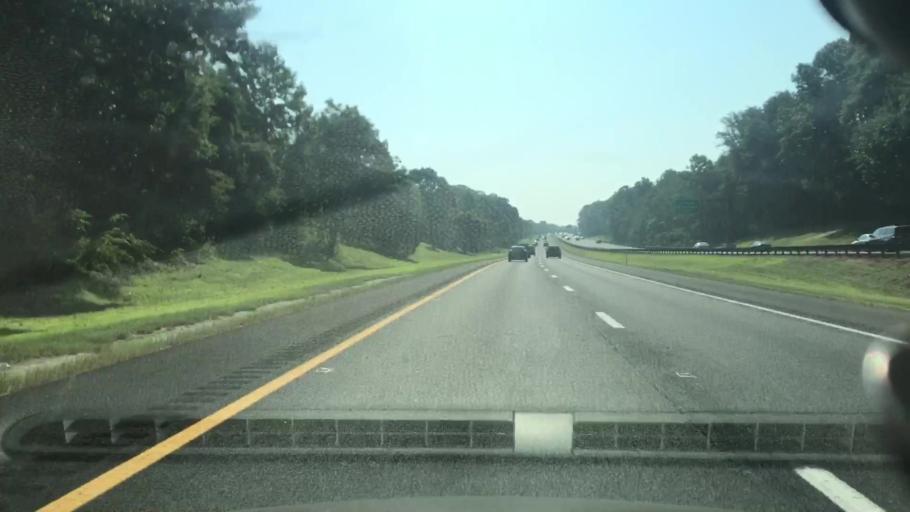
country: US
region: New Jersey
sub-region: Monmouth County
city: Strathmore
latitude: 40.3815
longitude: -74.1616
